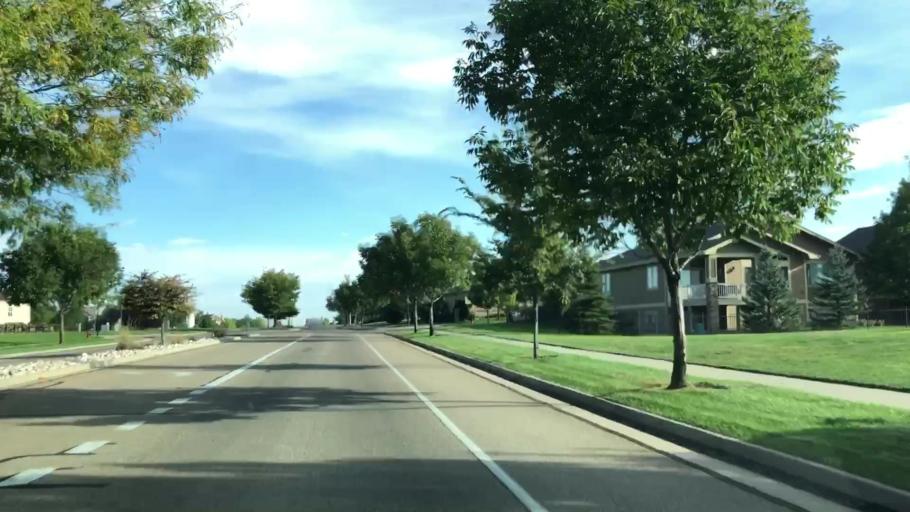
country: US
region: Colorado
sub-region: Weld County
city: Windsor
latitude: 40.4631
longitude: -104.9769
